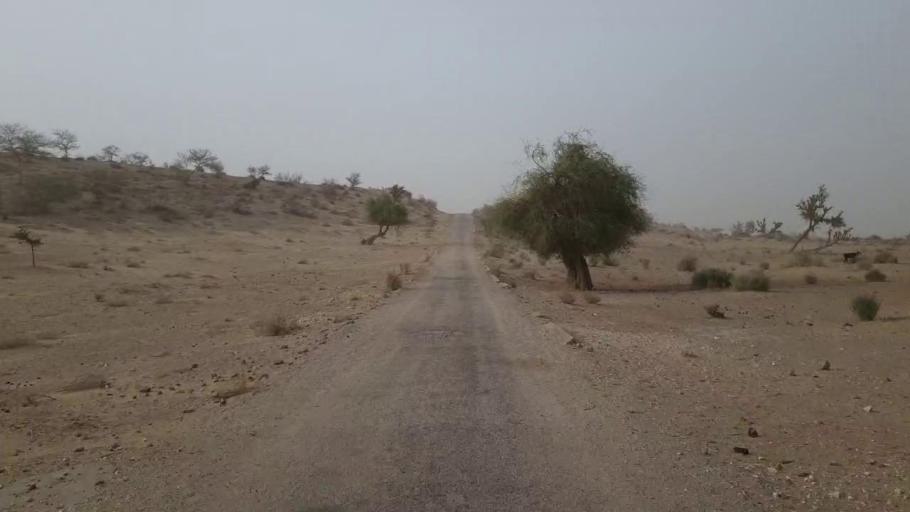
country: PK
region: Sindh
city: Islamkot
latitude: 24.5598
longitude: 70.3621
